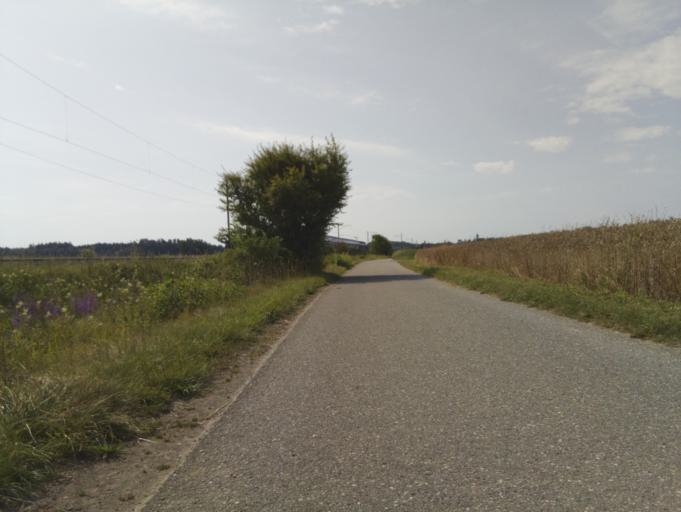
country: CH
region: Zurich
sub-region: Bezirk Andelfingen
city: Henggart
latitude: 47.5734
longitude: 8.6818
